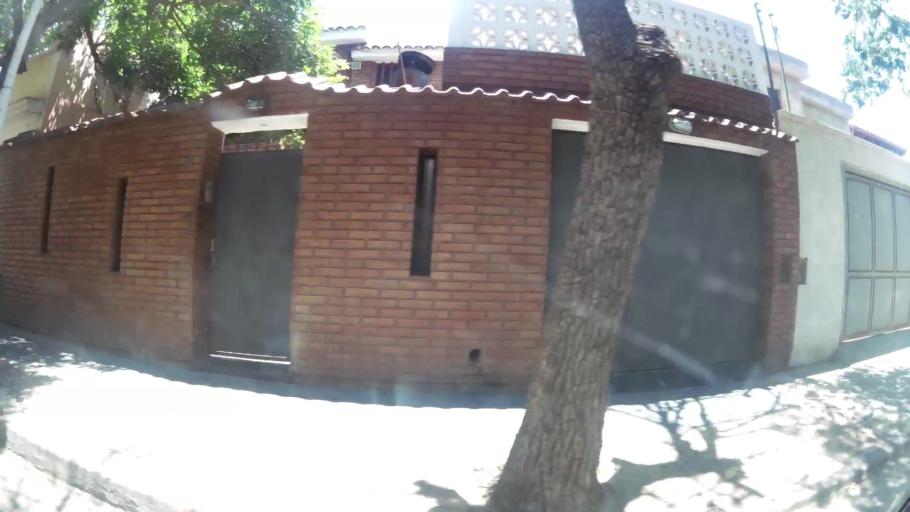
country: AR
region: Cordoba
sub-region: Departamento de Capital
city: Cordoba
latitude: -31.4048
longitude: -64.2048
